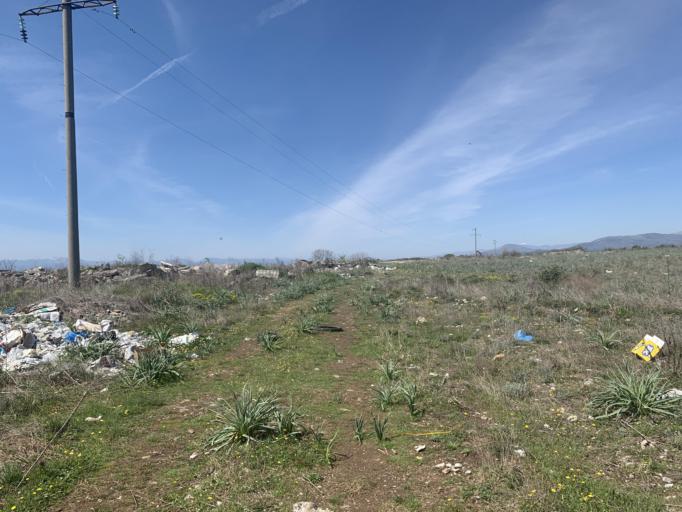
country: AL
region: Shkoder
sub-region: Rrethi i Malesia e Madhe
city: Koplik
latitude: 42.2298
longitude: 19.4355
